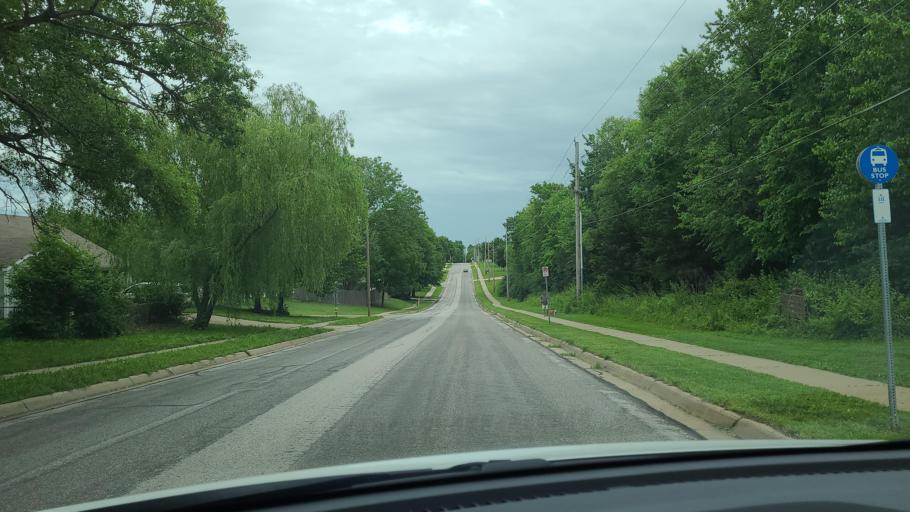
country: US
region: Kansas
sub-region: Douglas County
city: Lawrence
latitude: 38.9354
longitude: -95.2153
